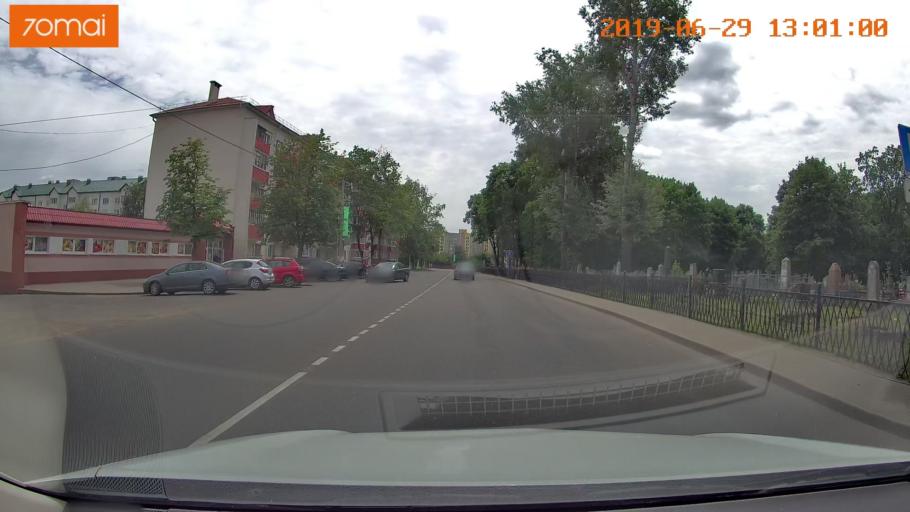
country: BY
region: Minsk
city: Slutsk
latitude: 53.0409
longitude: 27.5589
